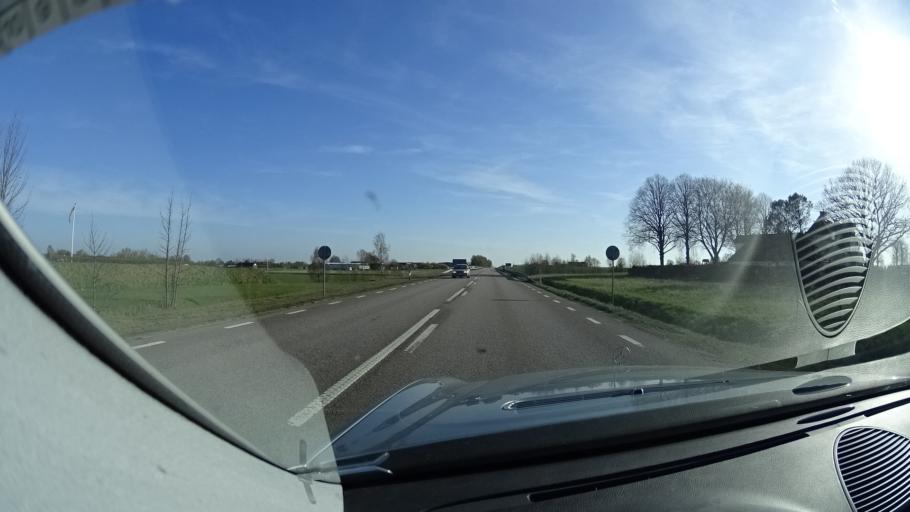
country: SE
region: Skane
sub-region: Bjuvs Kommun
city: Billesholm
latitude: 56.0092
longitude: 12.9552
